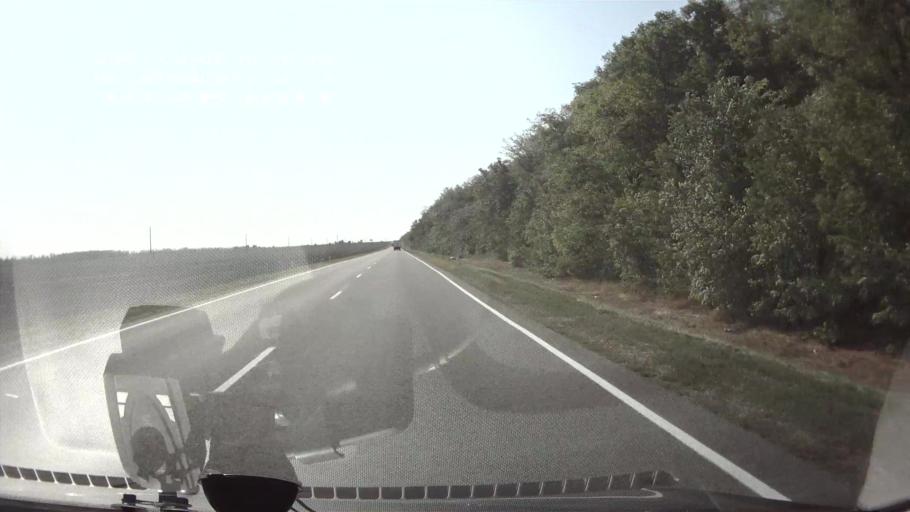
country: RU
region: Krasnodarskiy
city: Novopokrovskaya
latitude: 45.8914
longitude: 40.7210
